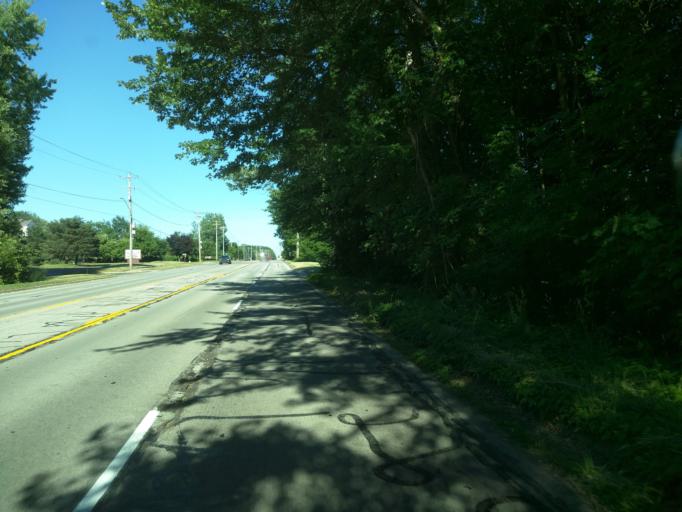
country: US
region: Michigan
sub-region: Eaton County
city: Waverly
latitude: 42.7338
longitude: -84.6379
